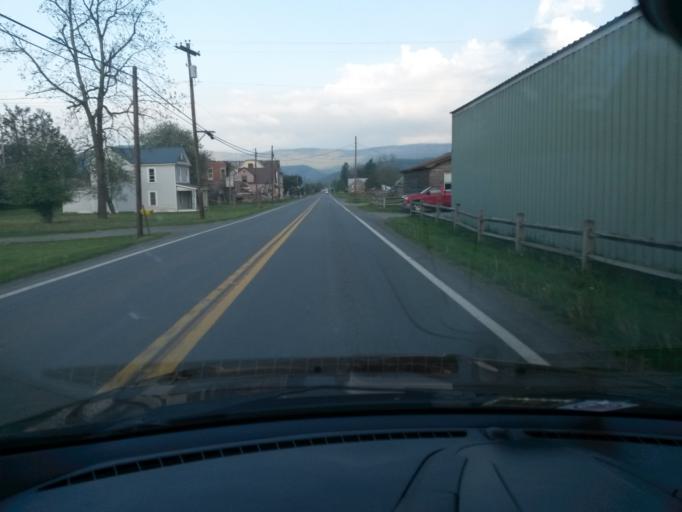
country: US
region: Virginia
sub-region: Highland County
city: Monterey
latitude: 38.5411
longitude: -79.7807
